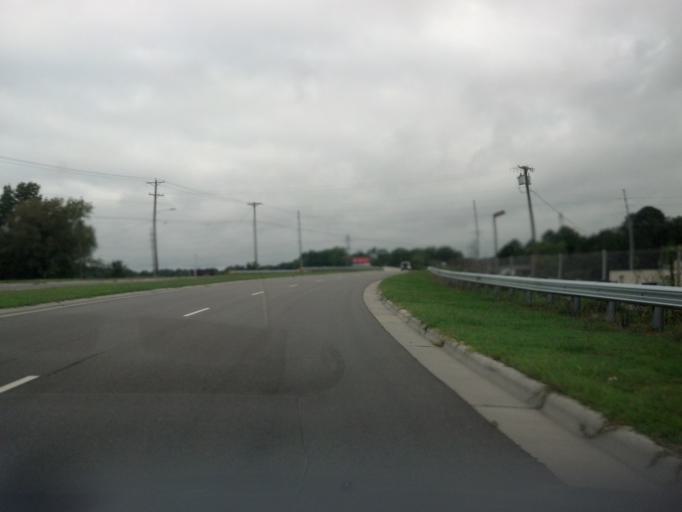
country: US
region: North Carolina
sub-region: Nash County
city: Rocky Mount
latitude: 35.9675
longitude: -77.8126
